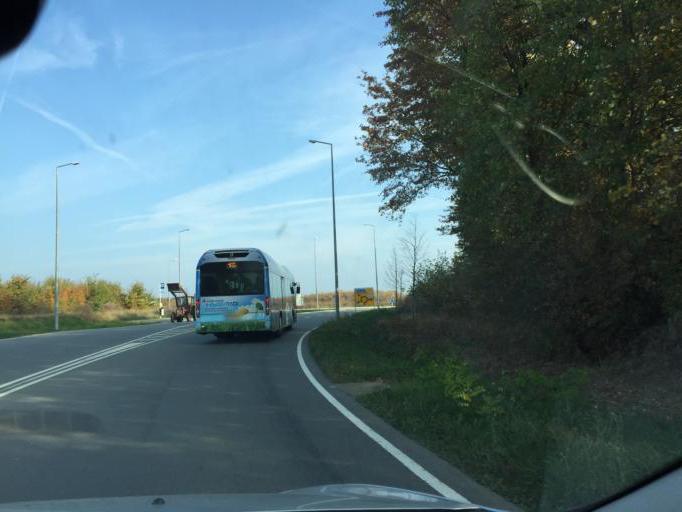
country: LU
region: Luxembourg
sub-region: Canton de Luxembourg
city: Contern
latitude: 49.5924
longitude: 6.2155
